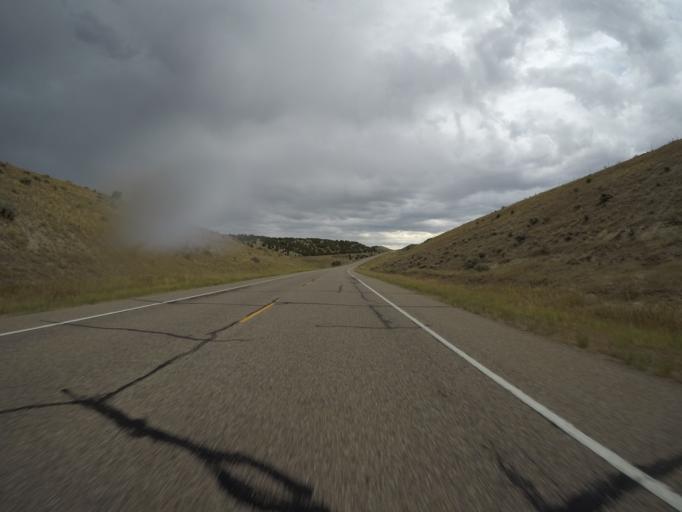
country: US
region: Colorado
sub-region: Rio Blanco County
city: Rangely
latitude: 40.3669
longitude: -108.4102
